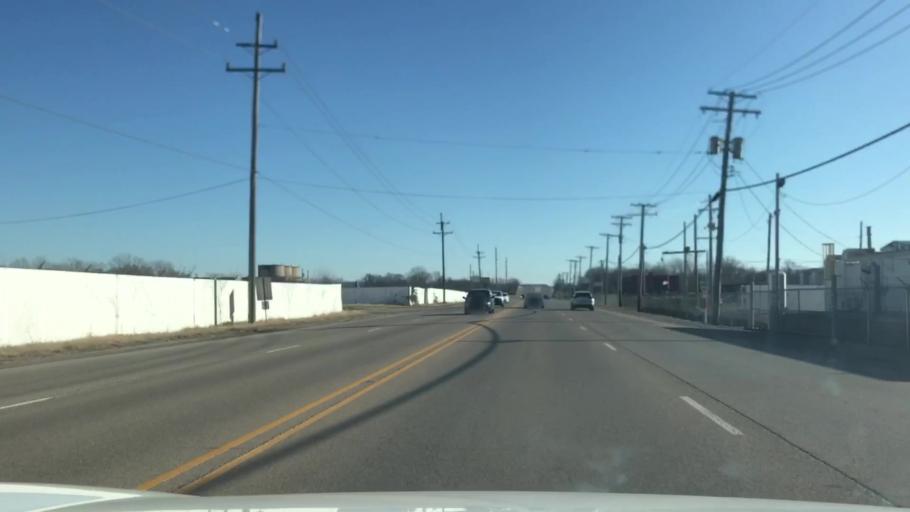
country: US
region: Illinois
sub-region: Saint Clair County
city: Alorton
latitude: 38.5983
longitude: -90.1261
